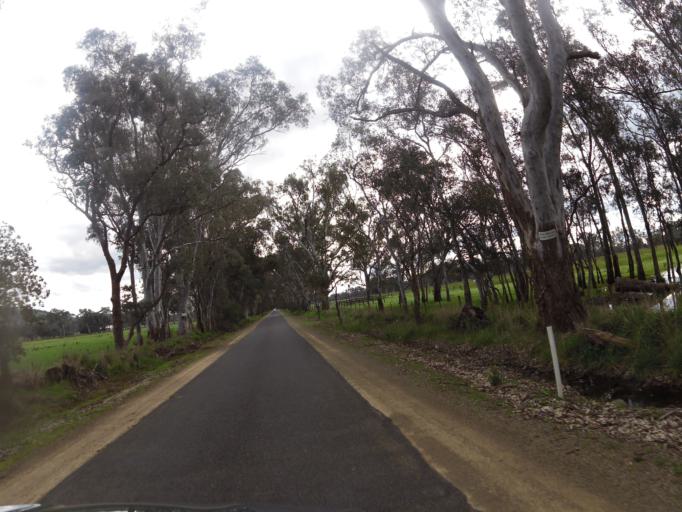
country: AU
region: Victoria
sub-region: Benalla
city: Benalla
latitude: -36.6806
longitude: 145.9751
